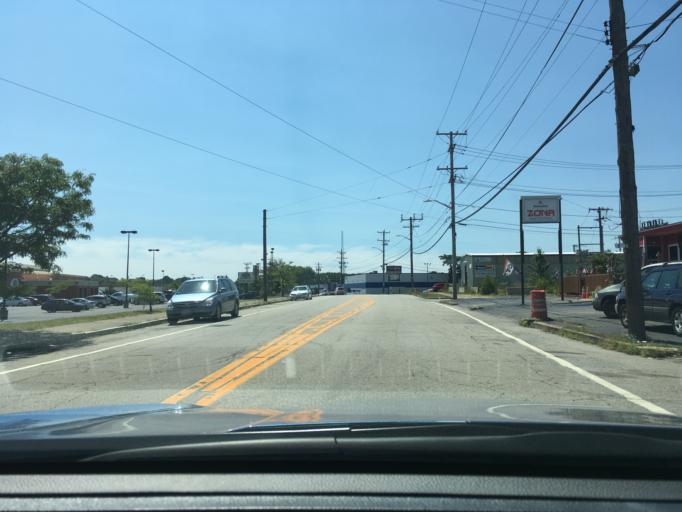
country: US
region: Rhode Island
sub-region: Providence County
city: Cranston
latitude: 41.7983
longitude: -71.4394
